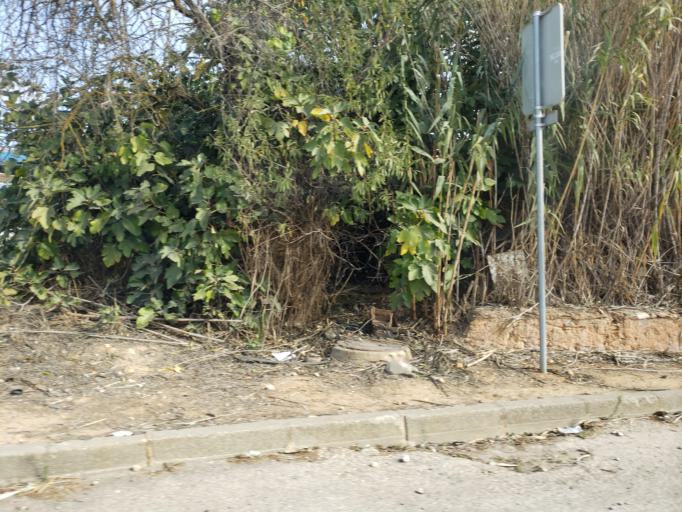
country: PT
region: Faro
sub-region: Portimao
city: Portimao
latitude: 37.1540
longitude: -8.5600
